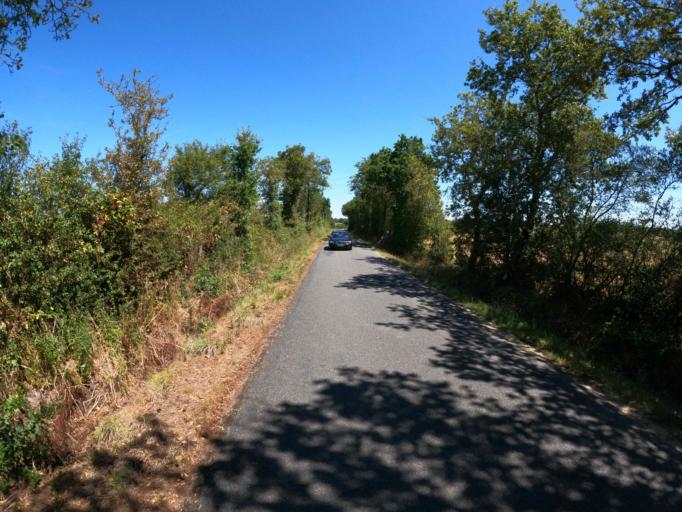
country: FR
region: Pays de la Loire
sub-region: Departement de la Loire-Atlantique
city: La Limouziniere
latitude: 46.9487
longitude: -1.6157
